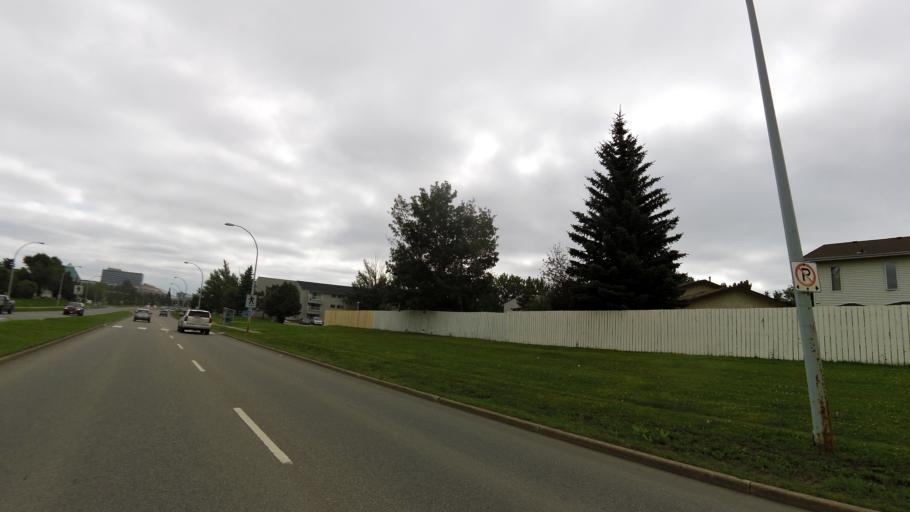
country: CA
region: Alberta
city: St. Albert
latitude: 53.5215
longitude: -113.6408
